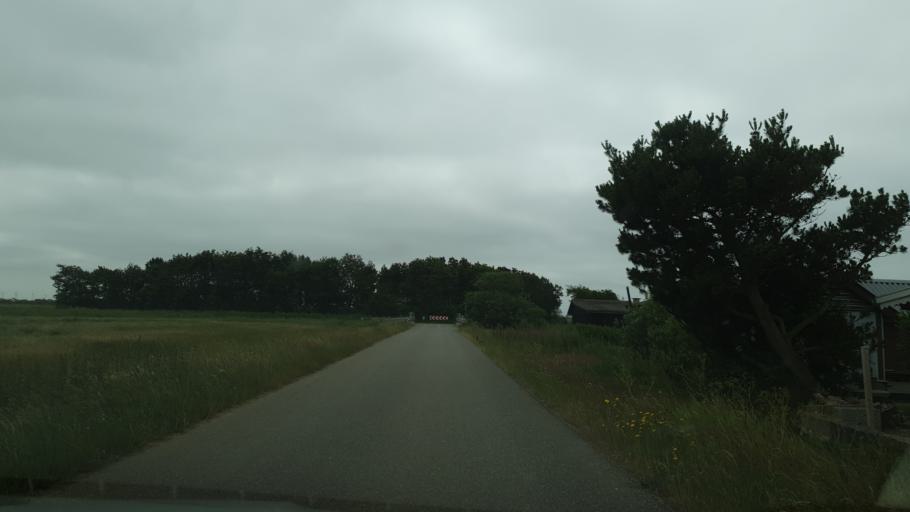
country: DK
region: Central Jutland
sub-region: Ringkobing-Skjern Kommune
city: Skjern
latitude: 55.9234
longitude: 8.4017
